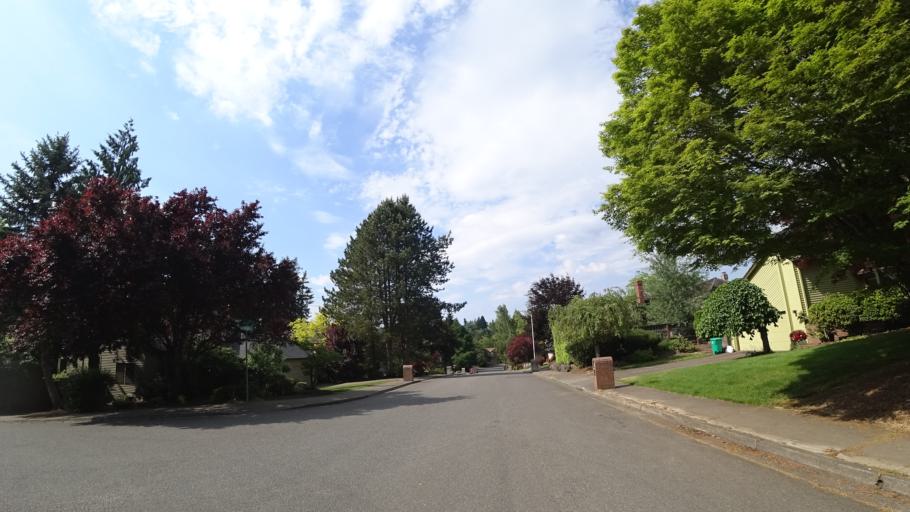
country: US
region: Oregon
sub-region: Washington County
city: Garden Home-Whitford
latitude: 45.4601
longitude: -122.7431
